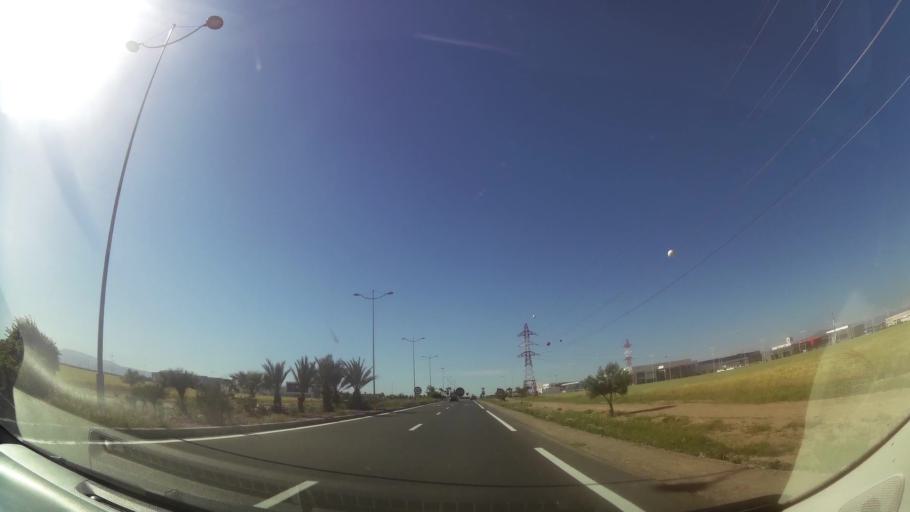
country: MA
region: Oriental
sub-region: Oujda-Angad
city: Oujda
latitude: 34.7653
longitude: -1.9400
